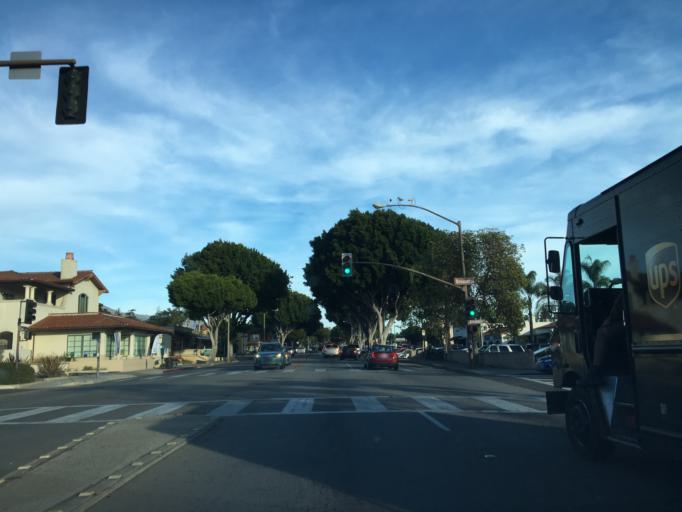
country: US
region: California
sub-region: Santa Barbara County
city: Mission Canyon
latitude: 34.4404
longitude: -119.7379
